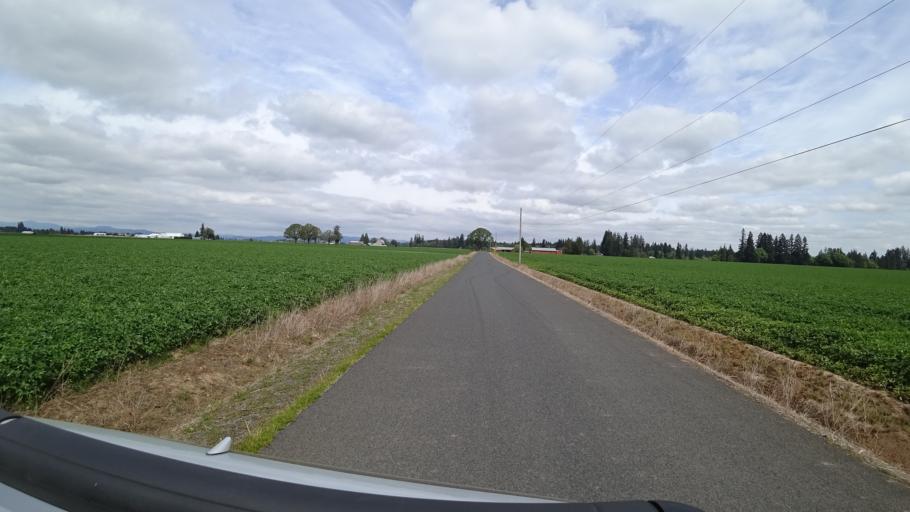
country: US
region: Oregon
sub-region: Washington County
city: Hillsboro
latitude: 45.5364
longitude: -123.0108
